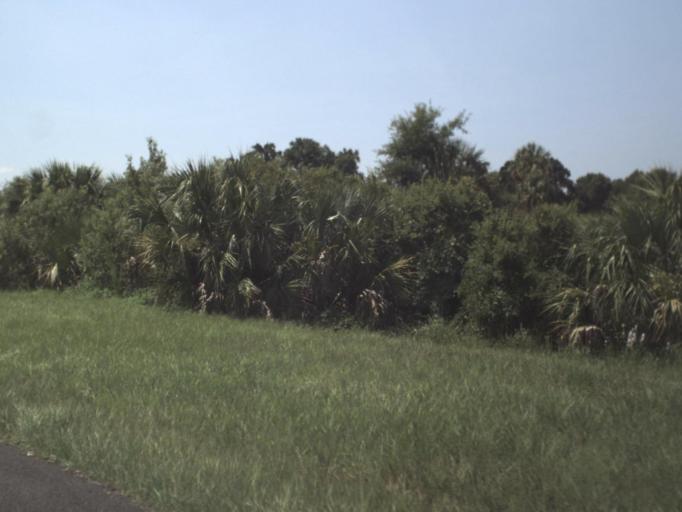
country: US
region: Florida
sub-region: Levy County
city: Inglis
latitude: 28.9857
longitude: -82.6455
